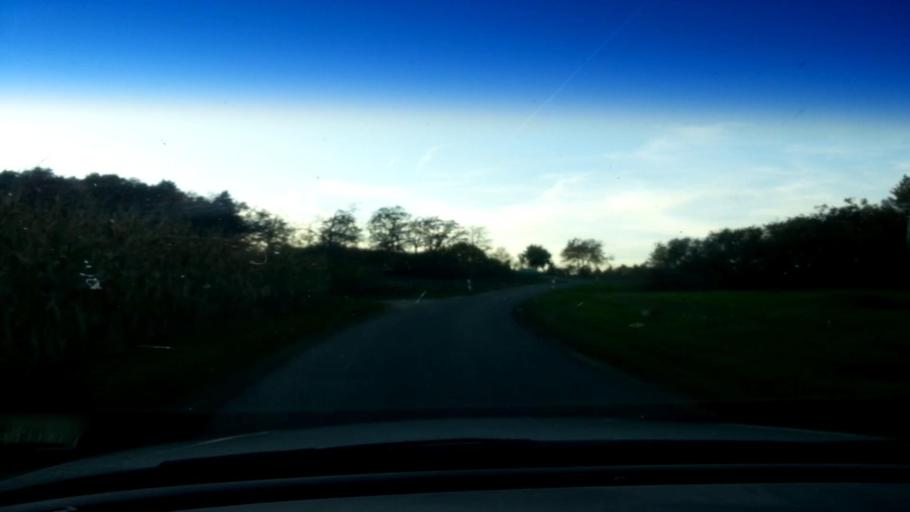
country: DE
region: Bavaria
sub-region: Upper Franconia
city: Unterleinleiter
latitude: 49.8395
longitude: 11.1769
